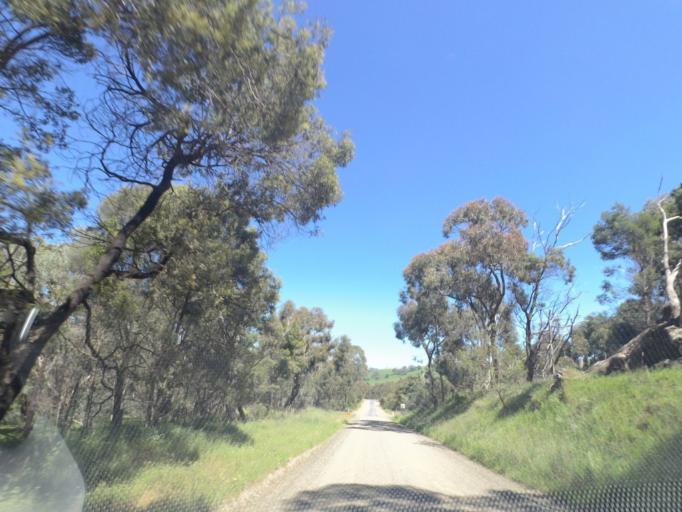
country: AU
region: Victoria
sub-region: Whittlesea
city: Whittlesea
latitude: -37.2837
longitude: 145.0039
